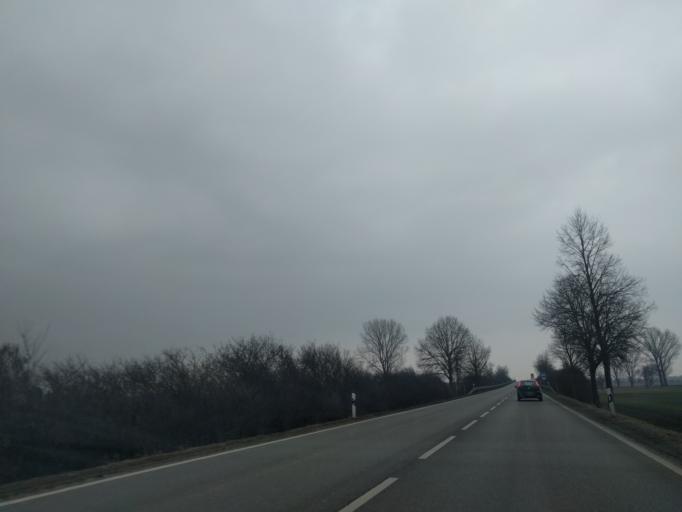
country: DE
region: Bavaria
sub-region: Swabia
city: Donauwoerth
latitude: 48.7018
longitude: 10.7877
